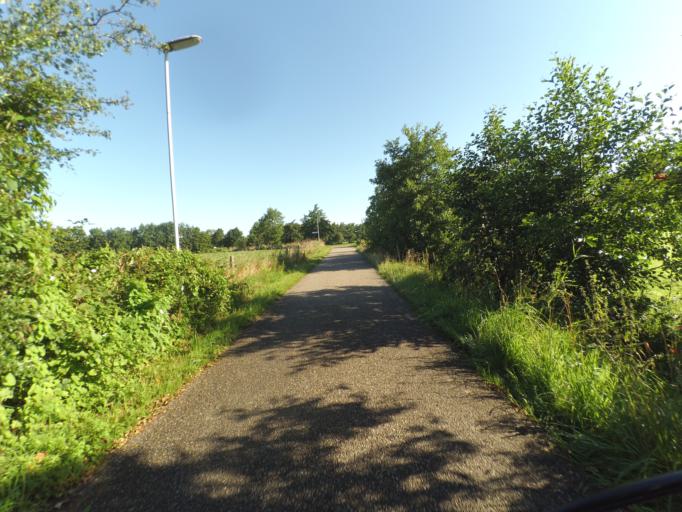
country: NL
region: Friesland
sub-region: Gemeente Achtkarspelen
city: Buitenpost
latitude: 53.2628
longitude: 6.1449
